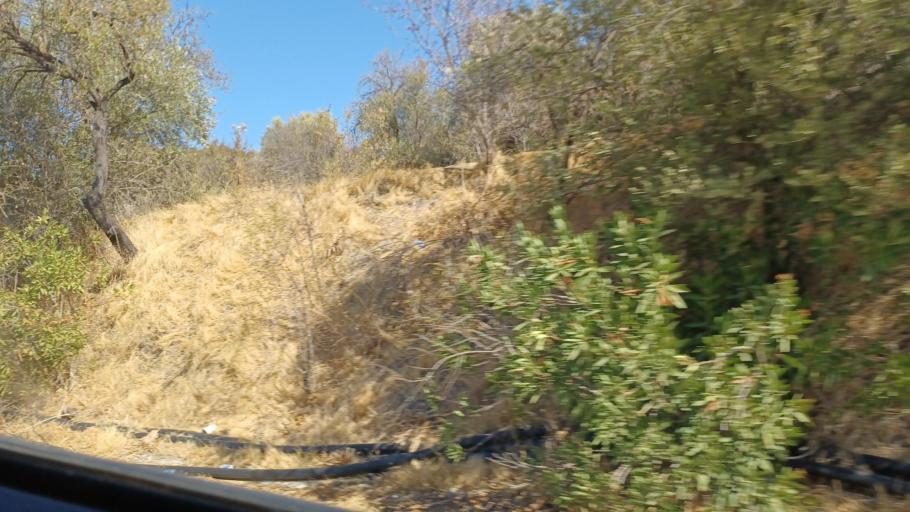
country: CY
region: Pafos
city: Mesogi
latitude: 34.9220
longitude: 32.5768
